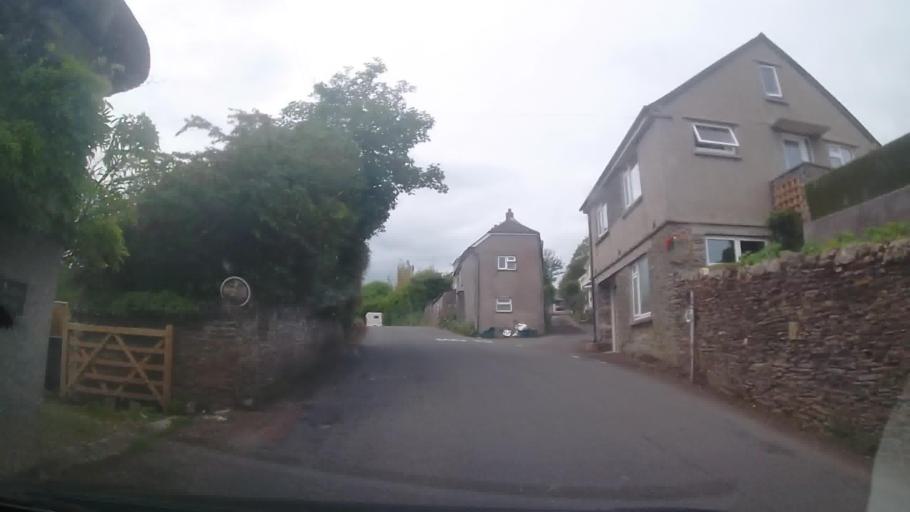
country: GB
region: England
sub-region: Devon
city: Kingsbridge
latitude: 50.2713
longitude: -3.7255
